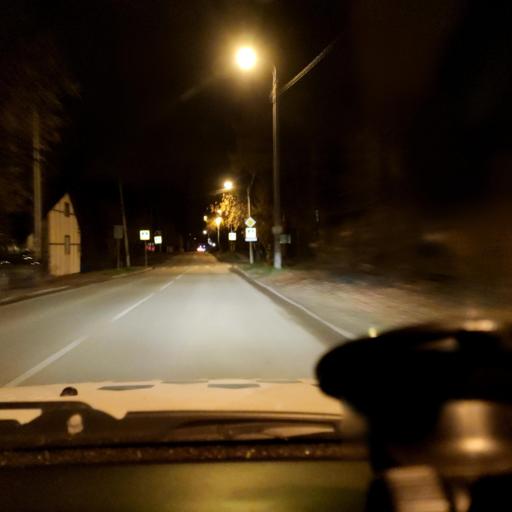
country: RU
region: Perm
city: Perm
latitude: 58.0239
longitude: 56.3352
